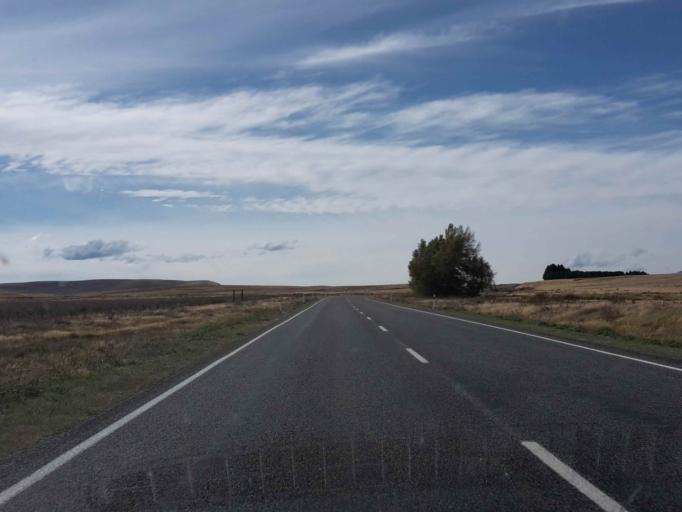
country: NZ
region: Canterbury
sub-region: Timaru District
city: Pleasant Point
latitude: -44.0403
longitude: 170.3819
